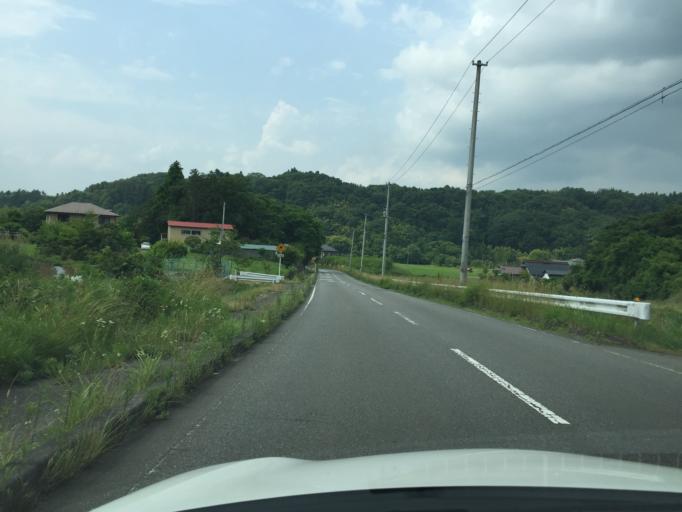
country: JP
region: Fukushima
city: Sukagawa
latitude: 37.3090
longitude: 140.4416
